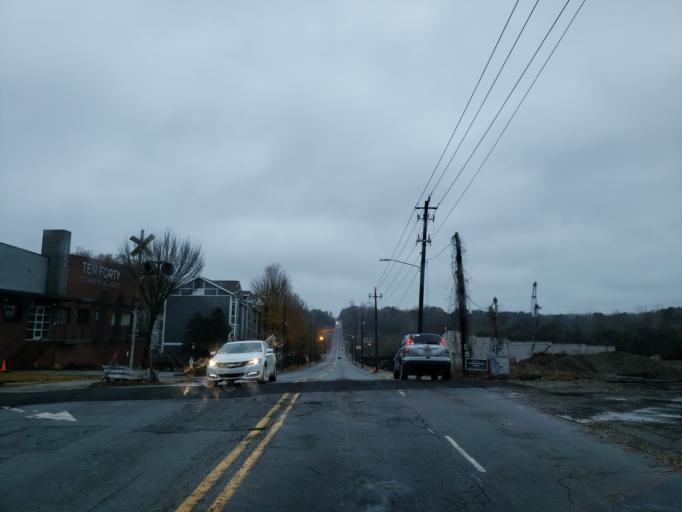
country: US
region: Georgia
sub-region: Fulton County
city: Atlanta
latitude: 33.7265
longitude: -84.3684
